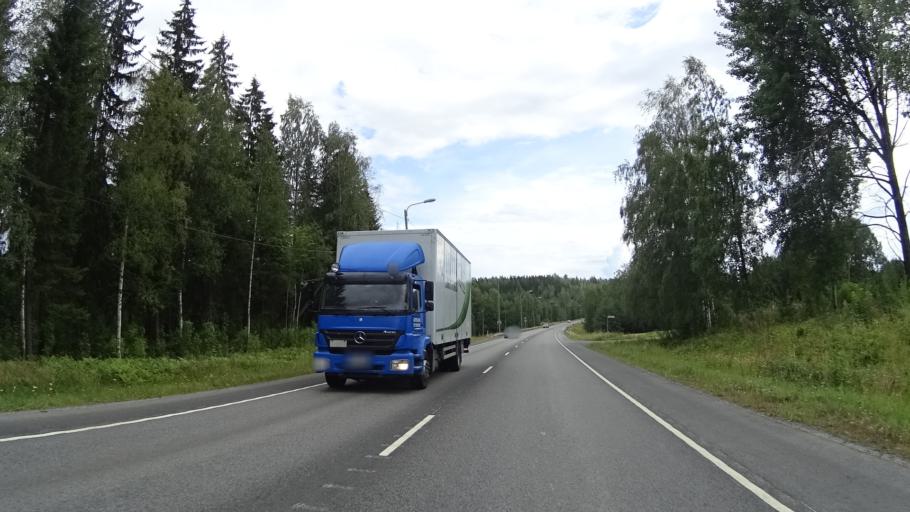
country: FI
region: Pirkanmaa
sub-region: Tampere
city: Kangasala
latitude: 61.4430
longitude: 24.1165
